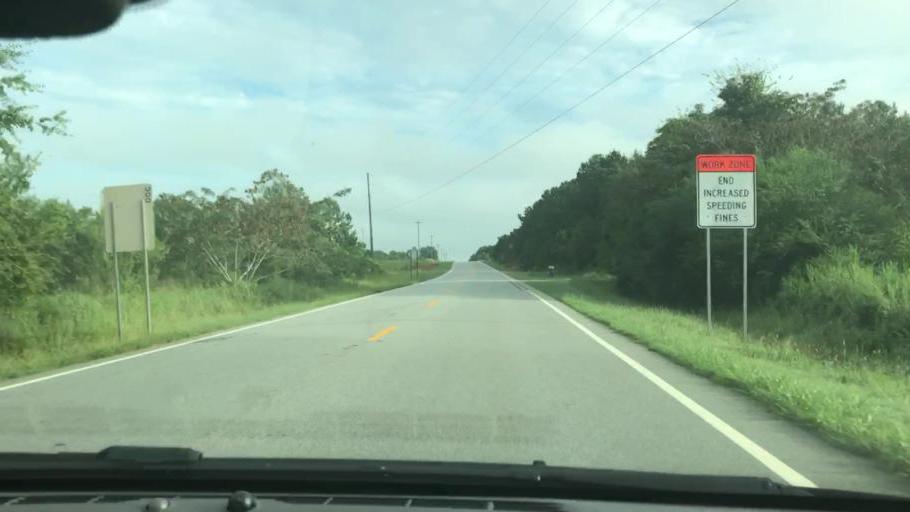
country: US
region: Georgia
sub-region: Quitman County
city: Georgetown
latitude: 31.7833
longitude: -85.0916
